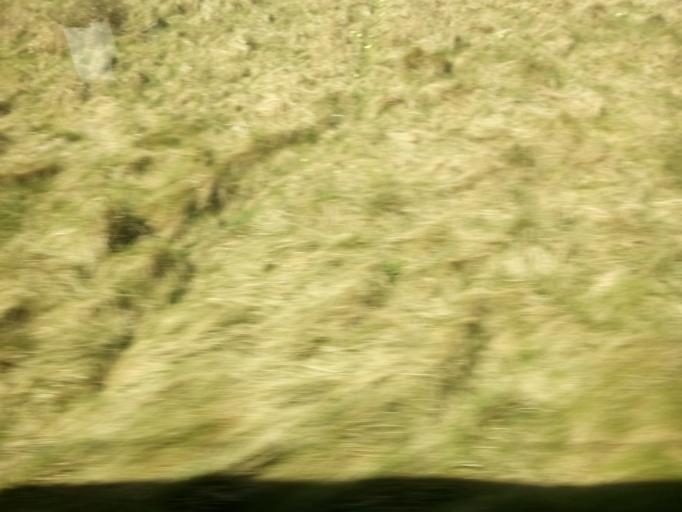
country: GB
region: Scotland
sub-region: The Scottish Borders
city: Eyemouth
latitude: 55.8242
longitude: -2.0532
